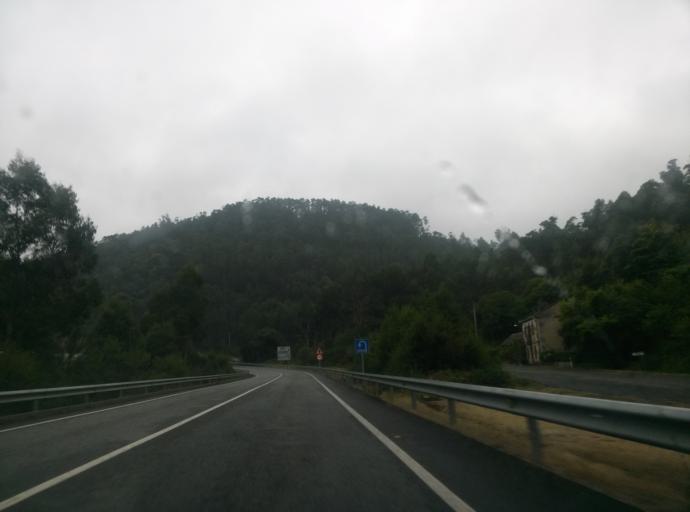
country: ES
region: Galicia
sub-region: Provincia de Lugo
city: Viveiro
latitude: 43.5679
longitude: -7.6441
